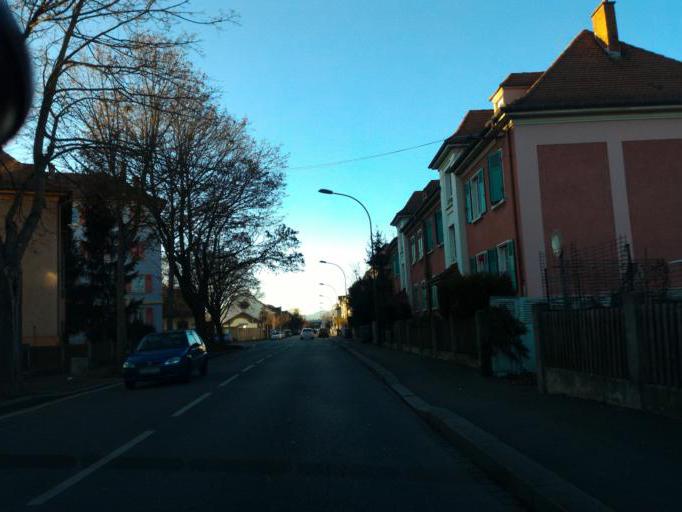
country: FR
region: Alsace
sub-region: Departement du Haut-Rhin
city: Riedisheim
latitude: 47.7613
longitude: 7.3621
